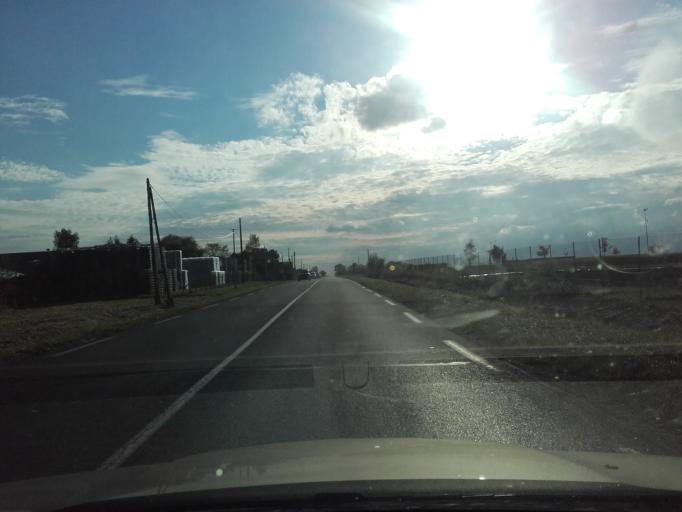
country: FR
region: Centre
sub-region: Departement d'Indre-et-Loire
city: Parcay-Meslay
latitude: 47.4713
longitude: 0.7533
